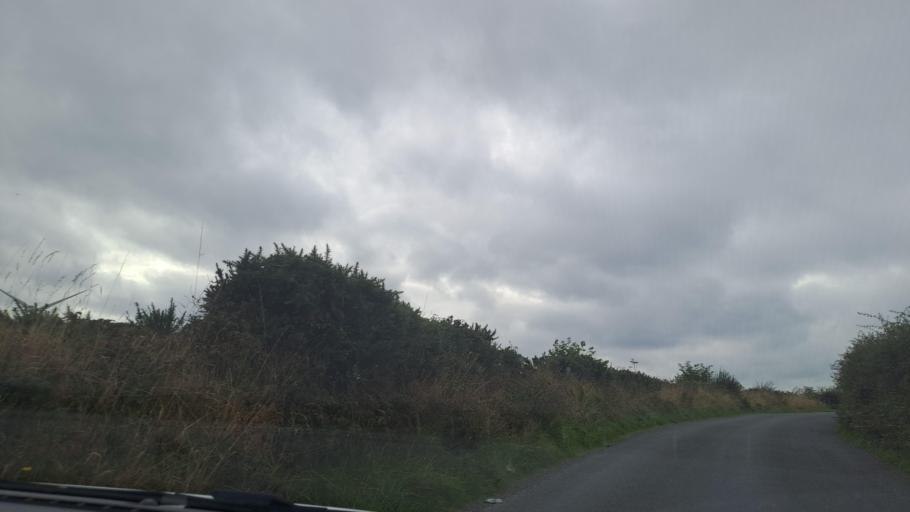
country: IE
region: Ulster
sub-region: An Cabhan
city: Bailieborough
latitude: 53.9541
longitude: -6.8867
